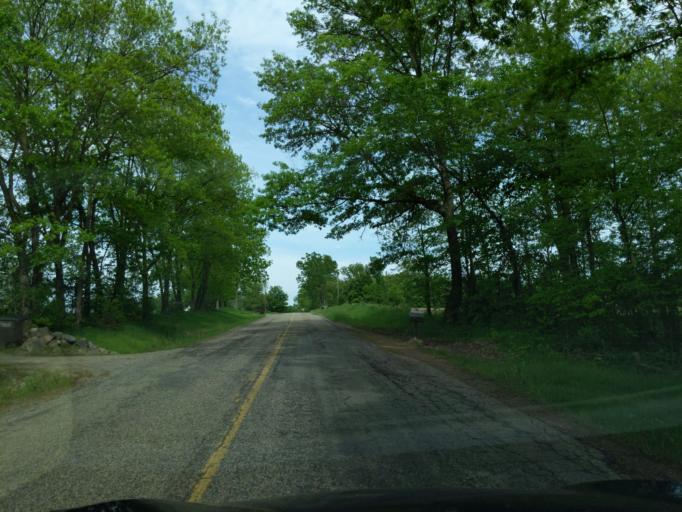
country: US
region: Michigan
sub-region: Ingham County
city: Leslie
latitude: 42.4167
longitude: -84.3442
